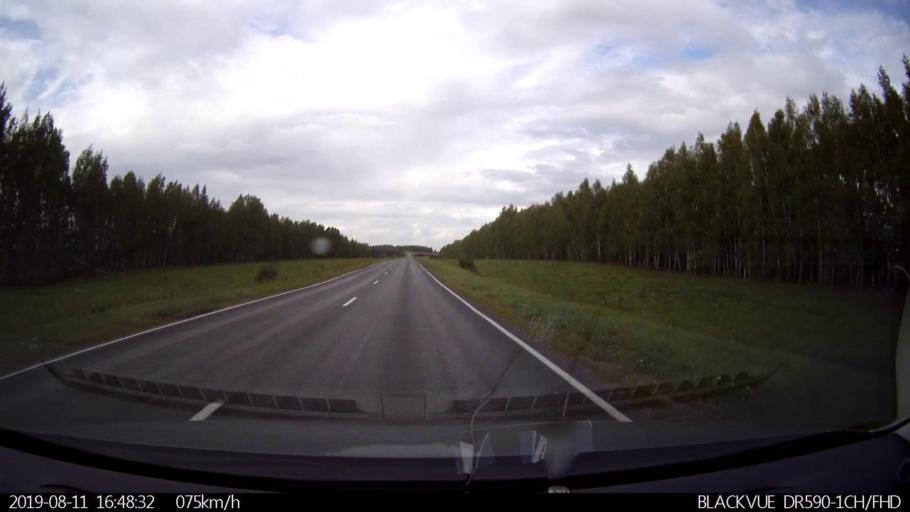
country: RU
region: Ulyanovsk
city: Mayna
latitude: 54.2102
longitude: 47.6926
